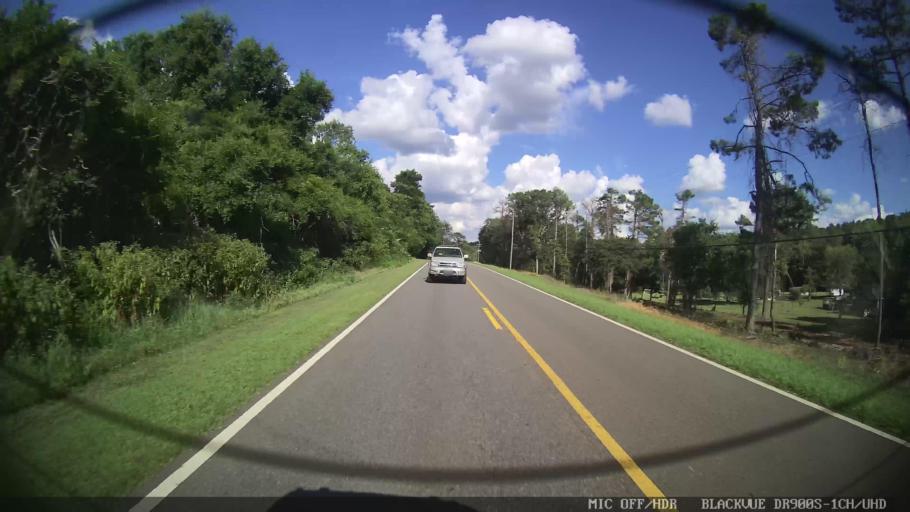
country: US
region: Georgia
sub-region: Bartow County
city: Euharlee
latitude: 34.1793
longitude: -85.0222
